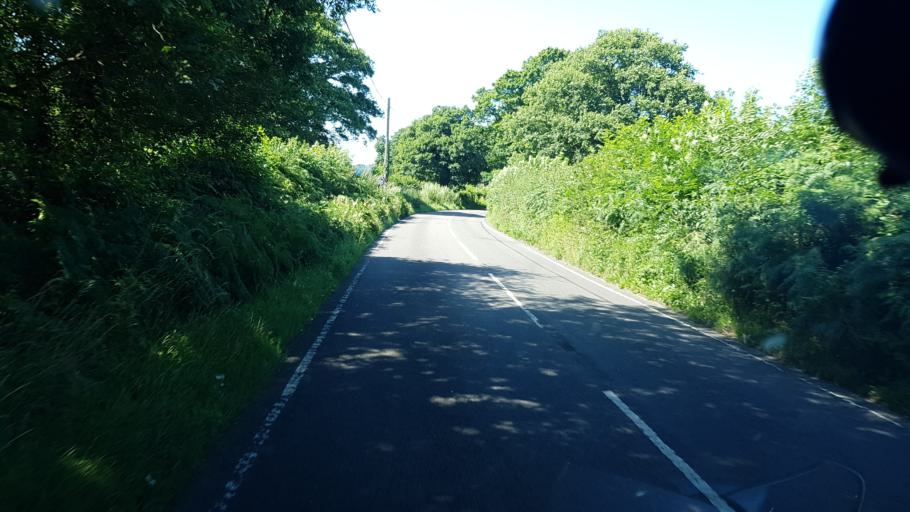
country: GB
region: England
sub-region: Kent
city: Edenbridge
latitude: 51.2185
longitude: 0.0947
